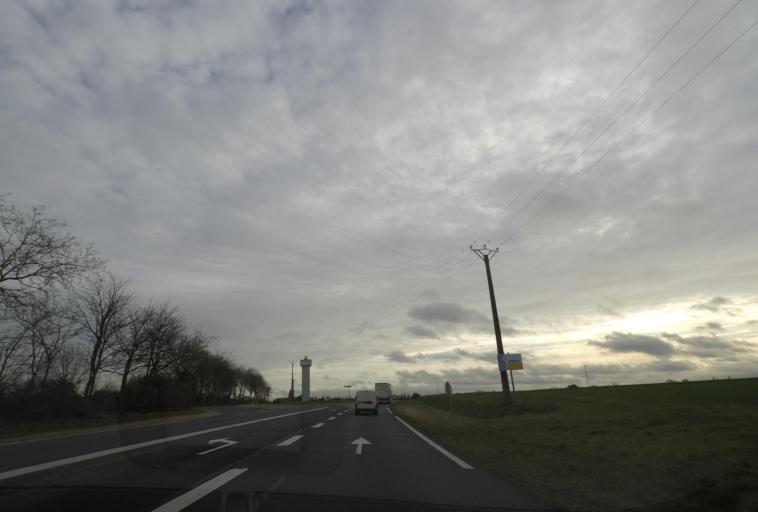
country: FR
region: Centre
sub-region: Departement du Loir-et-Cher
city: Sarge-sur-Braye
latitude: 47.9012
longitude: 0.9208
